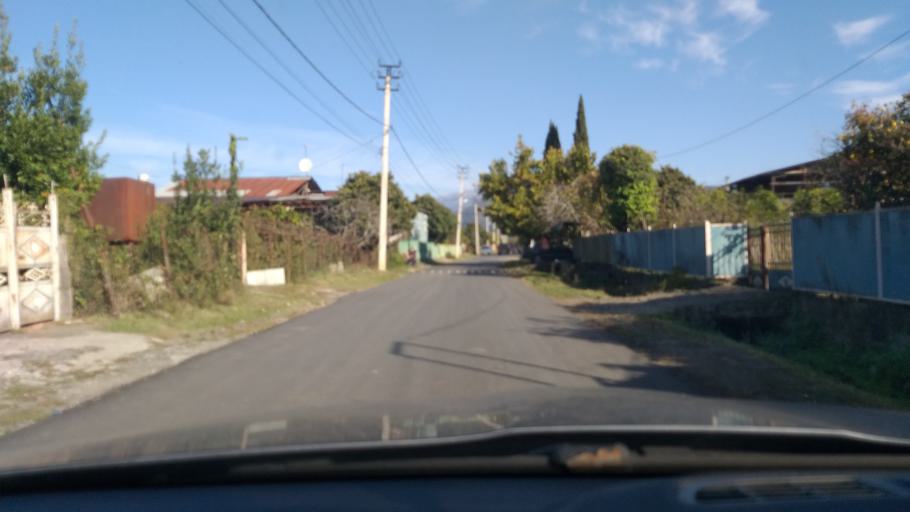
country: GE
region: Abkhazia
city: Sokhumi
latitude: 43.0179
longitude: 40.9660
